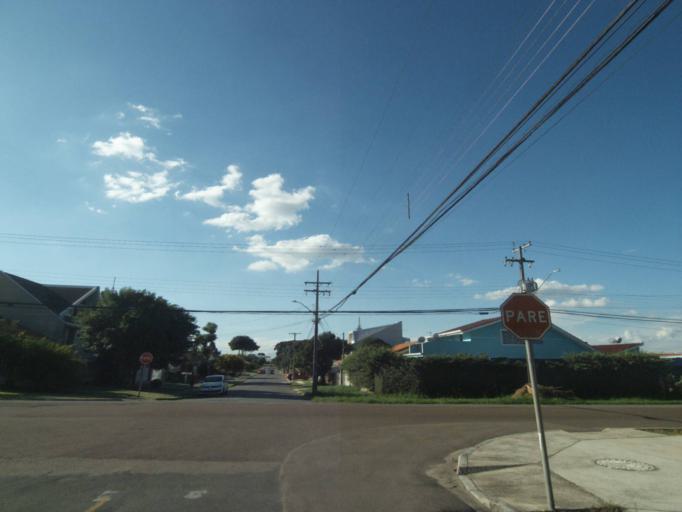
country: BR
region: Parana
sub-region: Pinhais
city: Pinhais
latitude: -25.4473
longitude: -49.2079
